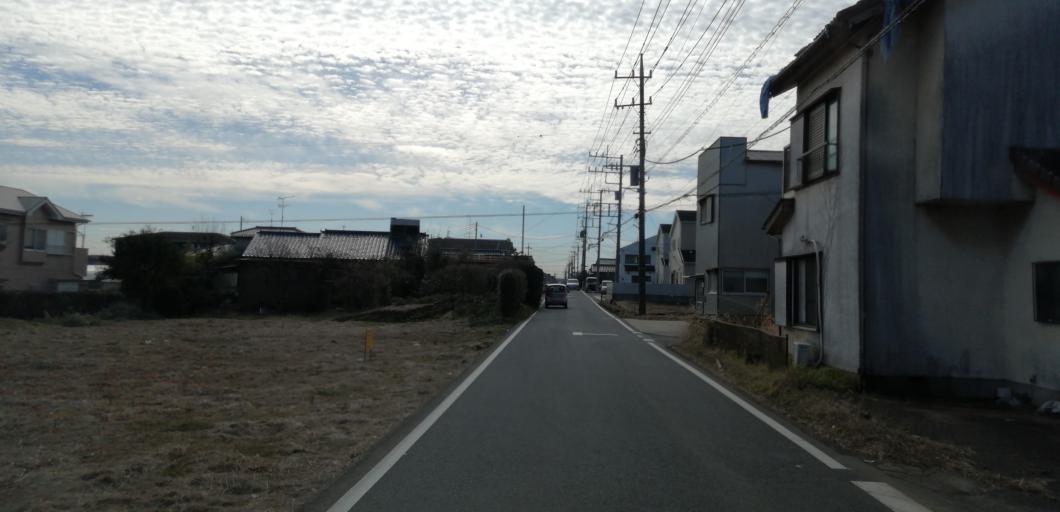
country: JP
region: Chiba
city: Narita
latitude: 35.7457
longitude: 140.3319
